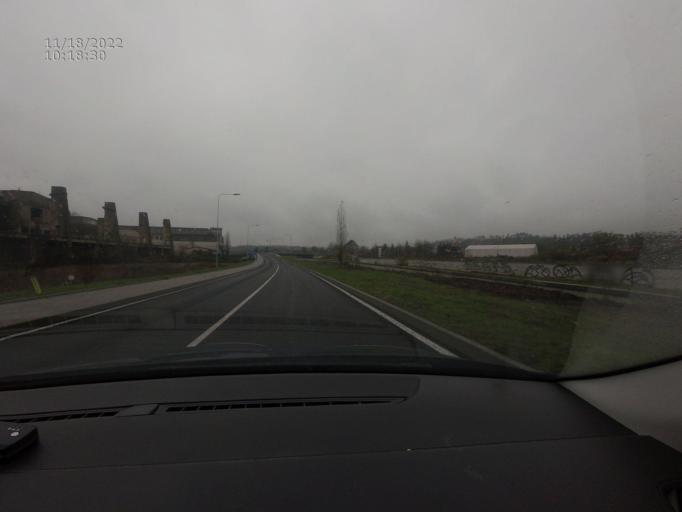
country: CZ
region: Central Bohemia
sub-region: Okres Beroun
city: Kraluv Dvur
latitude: 49.9424
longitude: 14.0351
